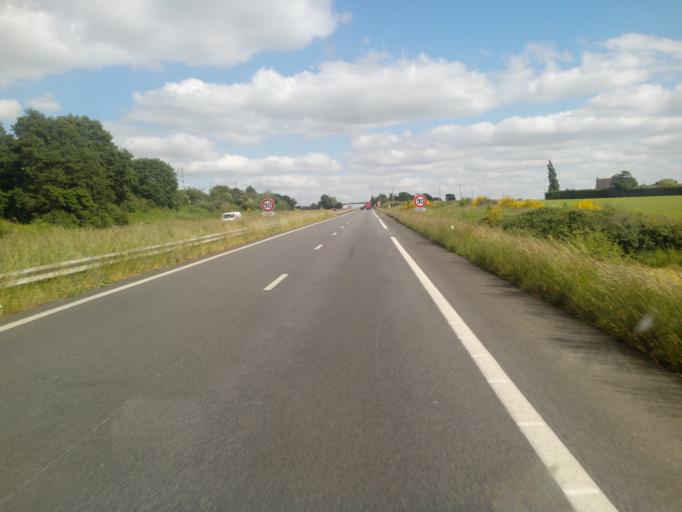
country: FR
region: Brittany
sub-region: Departement des Cotes-d'Armor
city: Sevignac
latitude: 48.3587
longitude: -2.3155
